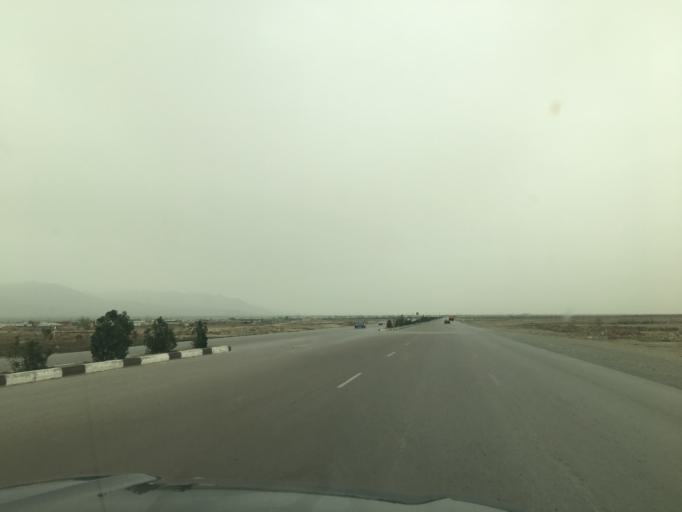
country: TM
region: Ahal
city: Baharly
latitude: 38.3762
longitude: 57.5089
